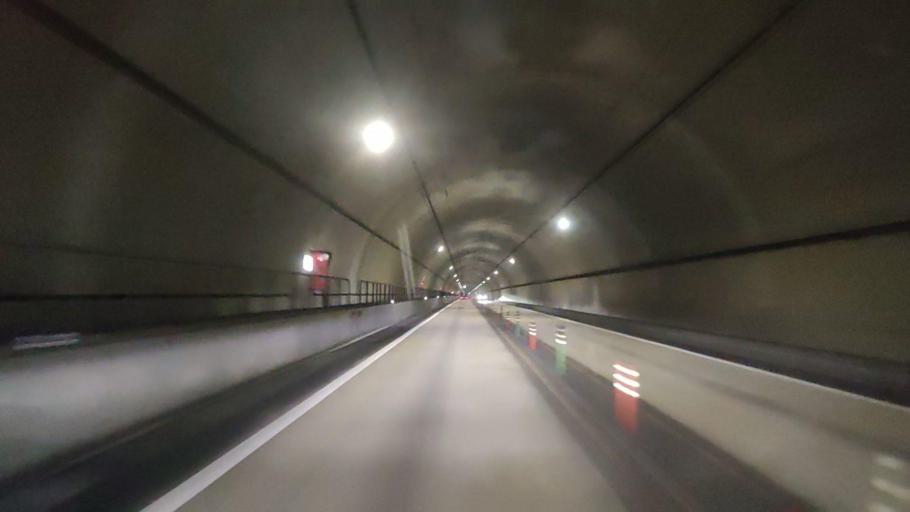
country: JP
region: Wakayama
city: Tanabe
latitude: 33.5437
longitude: 135.5252
